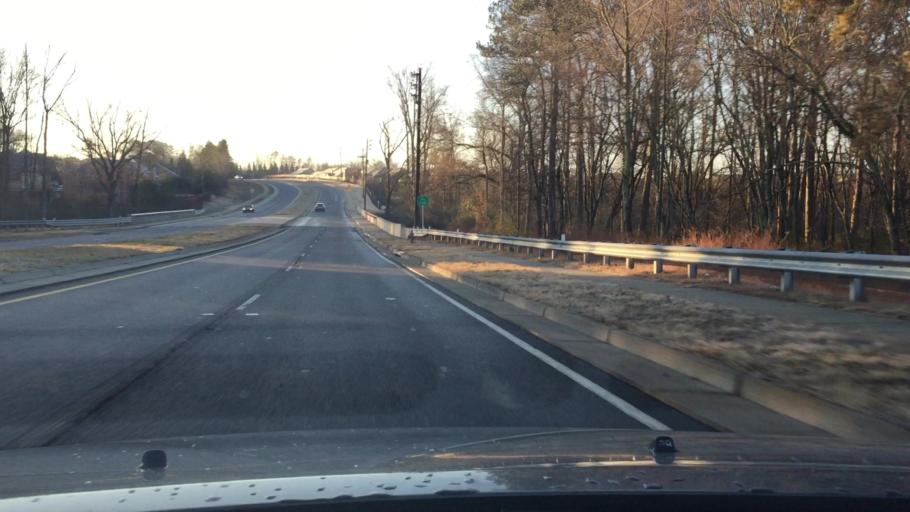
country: US
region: Georgia
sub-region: Forsyth County
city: Cumming
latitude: 34.1809
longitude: -84.1936
